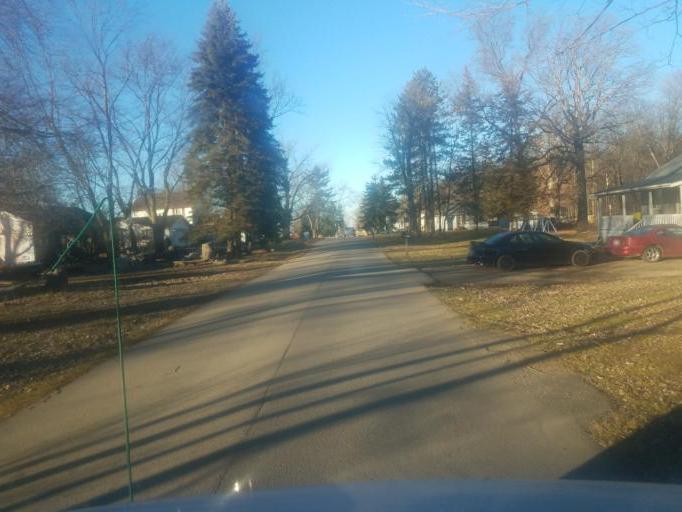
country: US
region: Ohio
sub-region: Richland County
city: Mansfield
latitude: 40.7788
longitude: -82.5482
